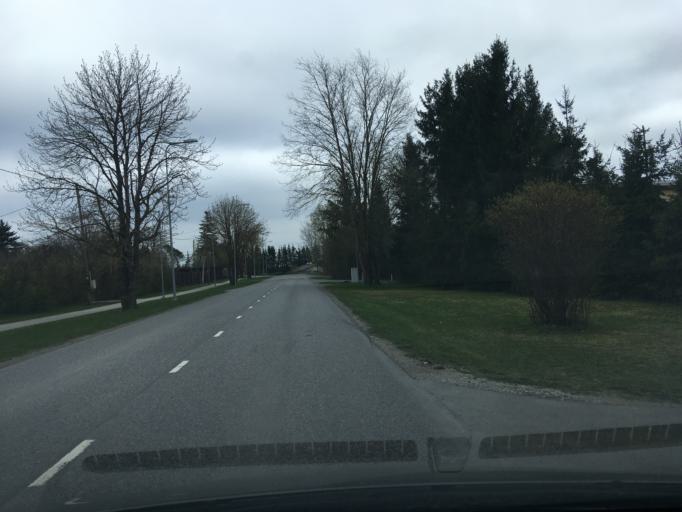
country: EE
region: Harju
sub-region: Rae vald
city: Jueri
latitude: 59.3527
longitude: 24.8956
